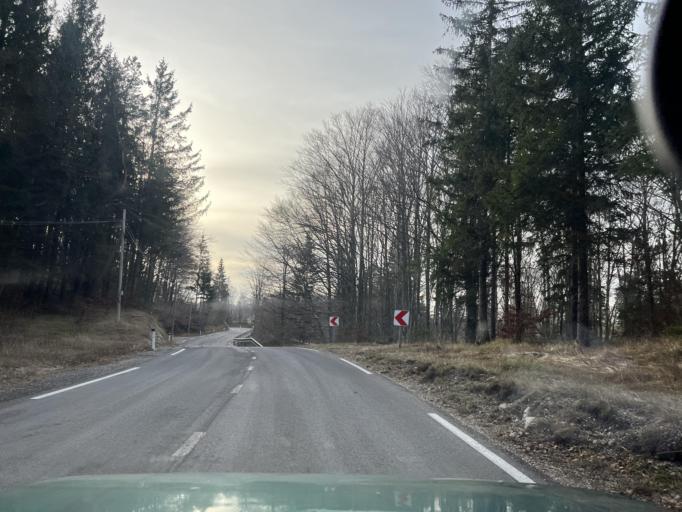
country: SI
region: Nova Gorica
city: Sempas
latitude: 45.9819
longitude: 13.7539
